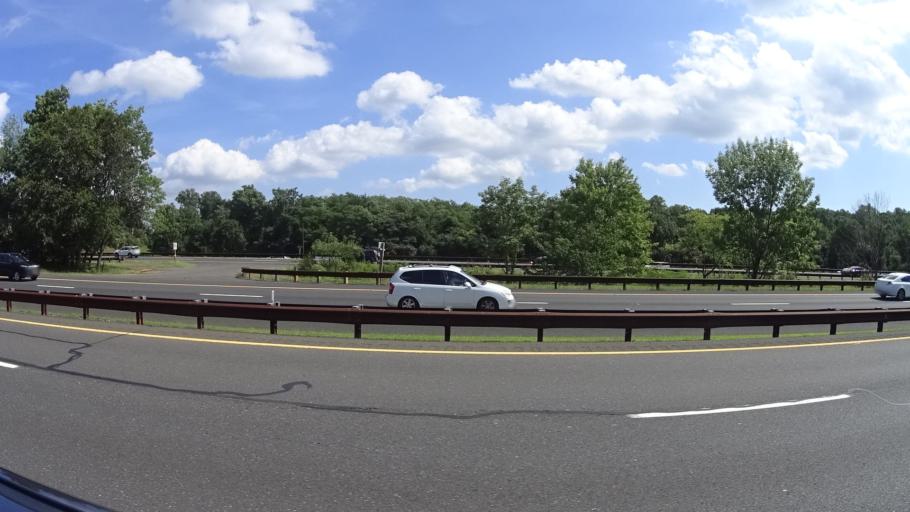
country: US
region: New Jersey
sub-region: Monmouth County
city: Lincroft
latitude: 40.3739
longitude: -74.1469
